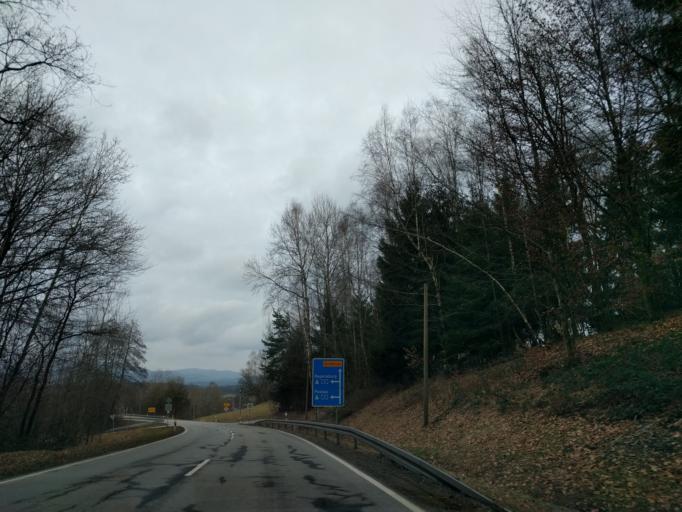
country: DE
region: Bavaria
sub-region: Lower Bavaria
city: Iggensbach
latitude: 48.7252
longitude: 13.1336
